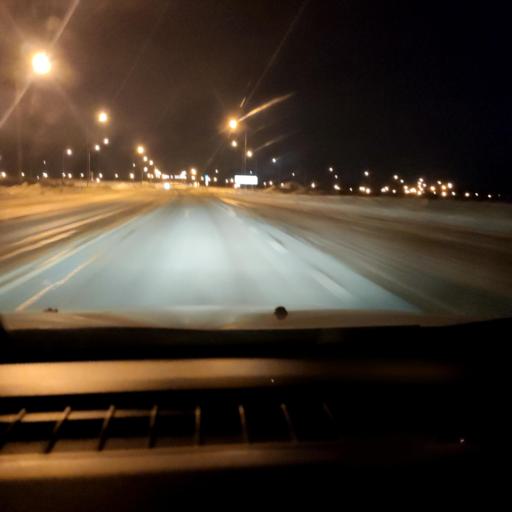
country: RU
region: Samara
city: Smyshlyayevka
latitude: 53.1524
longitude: 50.3960
